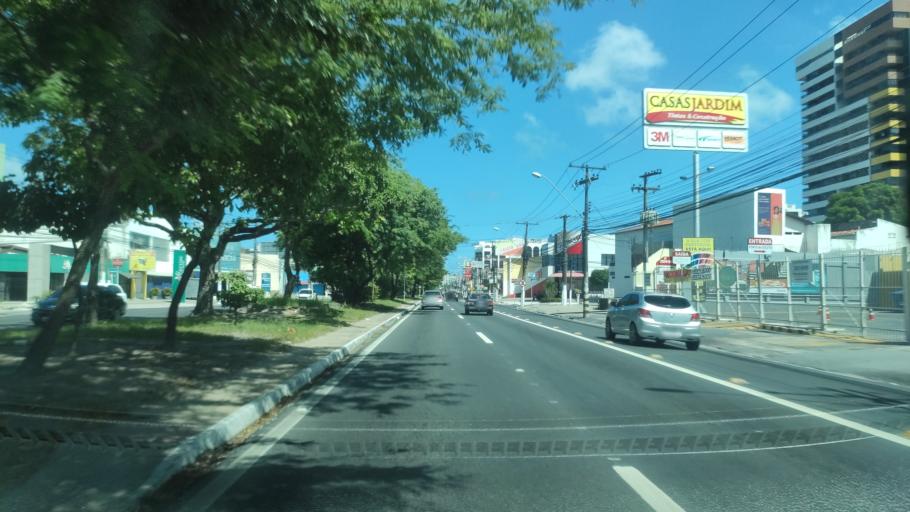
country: BR
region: Alagoas
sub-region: Maceio
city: Maceio
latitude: -9.6417
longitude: -35.7352
